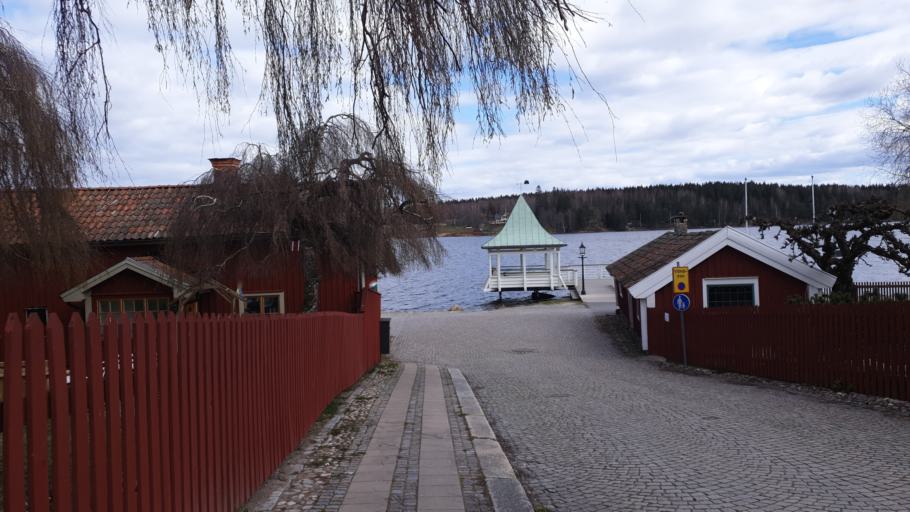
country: SE
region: OErebro
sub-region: Nora Kommun
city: Nora
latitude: 59.5191
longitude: 15.0433
